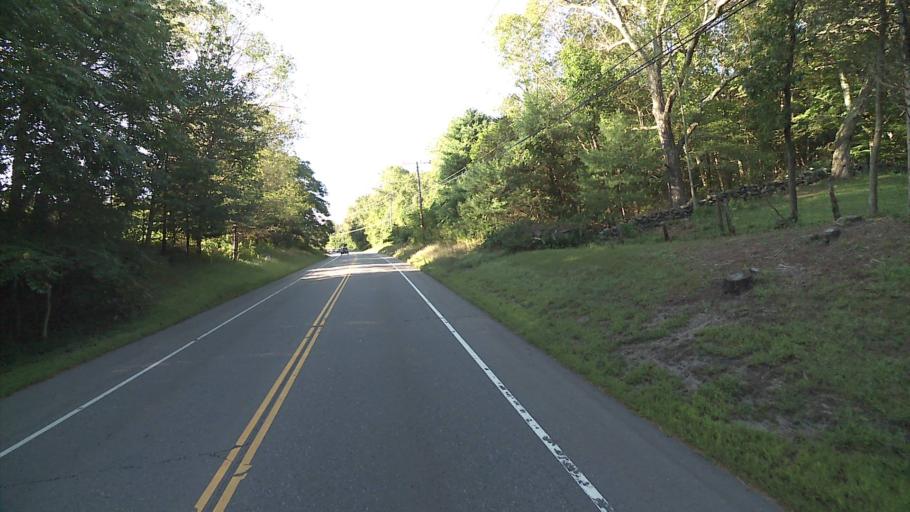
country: US
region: Connecticut
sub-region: Windham County
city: South Windham
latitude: 41.6633
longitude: -72.1603
